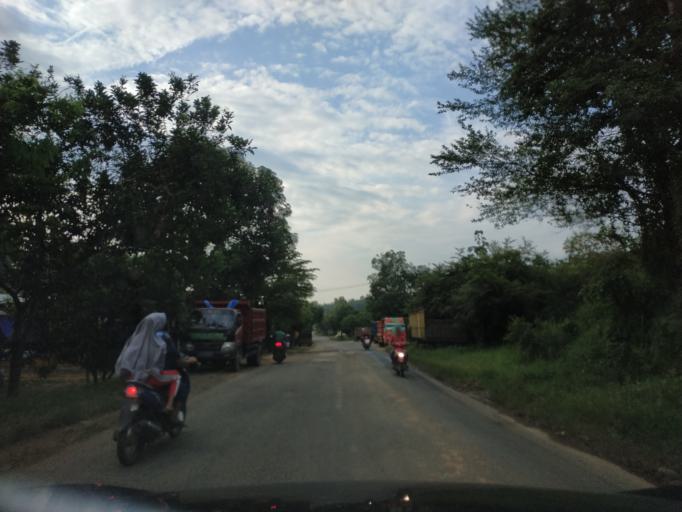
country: ID
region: Central Java
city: Ngampel
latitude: -6.8959
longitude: 111.4400
